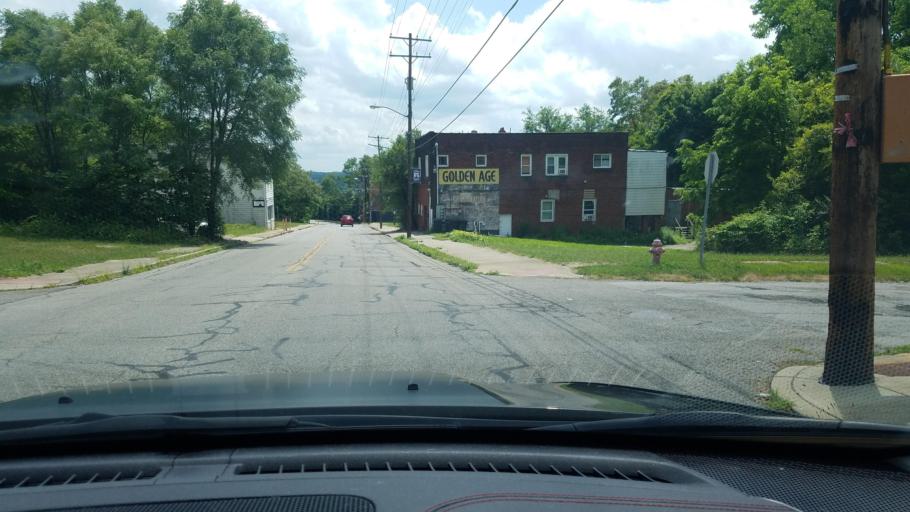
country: US
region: Ohio
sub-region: Mahoning County
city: Campbell
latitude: 41.0726
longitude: -80.5934
